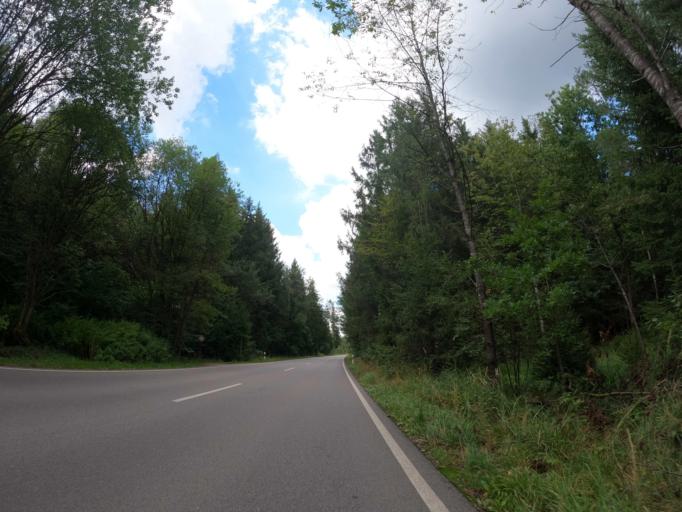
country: DE
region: Bavaria
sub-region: Upper Bavaria
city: Ottobrunn
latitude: 48.0399
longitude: 11.6724
